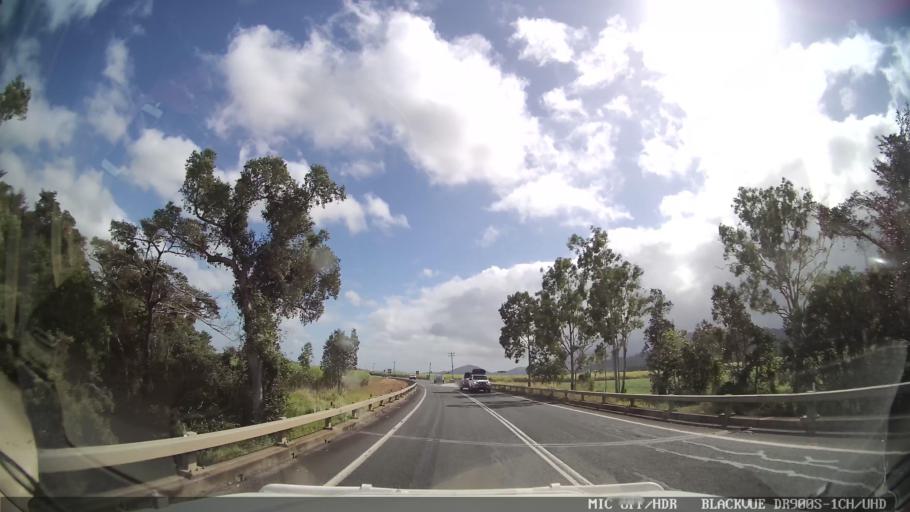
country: AU
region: Queensland
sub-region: Whitsunday
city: Proserpine
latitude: -20.3506
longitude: 148.5560
